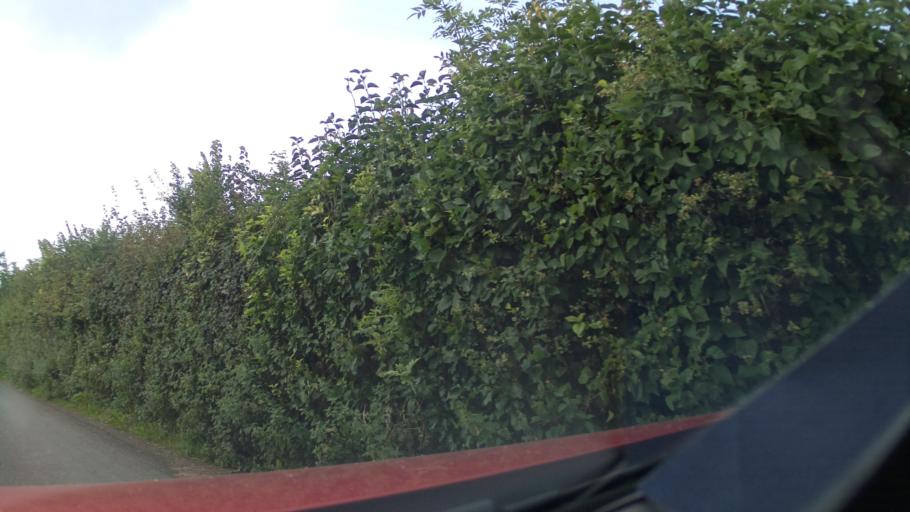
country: GB
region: England
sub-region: Somerset
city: Evercreech
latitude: 51.1486
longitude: -2.4919
